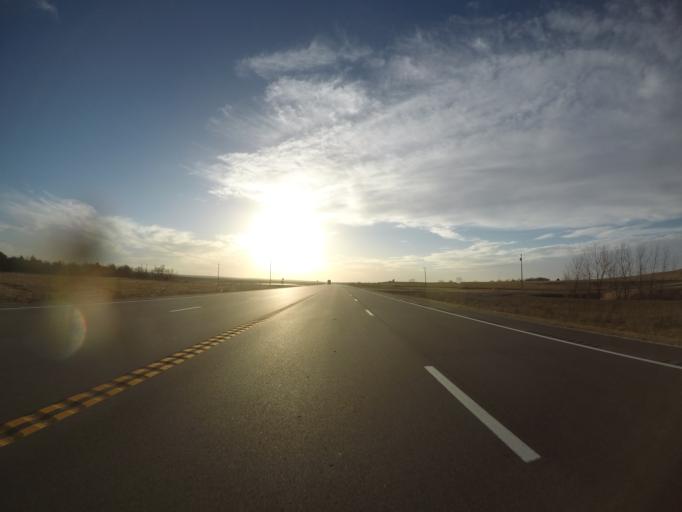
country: US
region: Kansas
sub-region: Chase County
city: Cottonwood Falls
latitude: 38.4020
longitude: -96.5009
